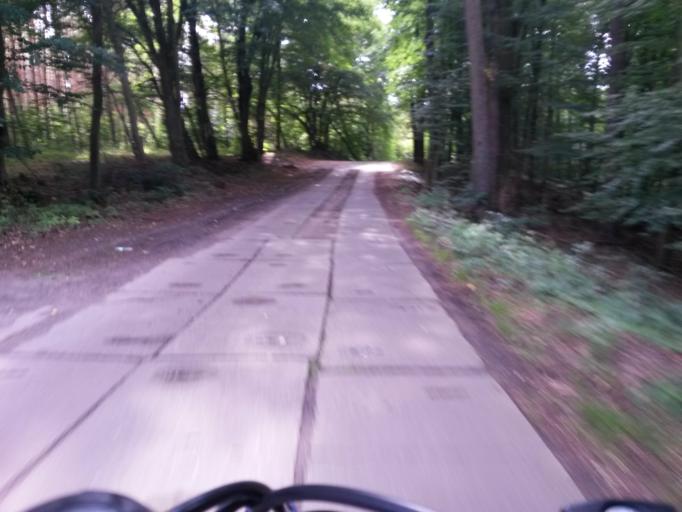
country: DE
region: Brandenburg
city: Althuttendorf
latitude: 53.0174
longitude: 13.8670
